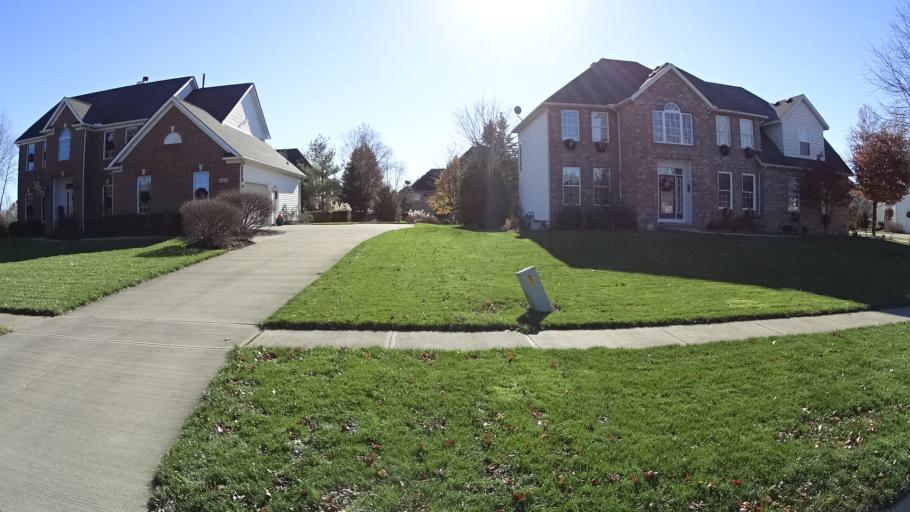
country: US
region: Ohio
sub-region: Lorain County
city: Avon
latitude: 41.4389
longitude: -82.0298
